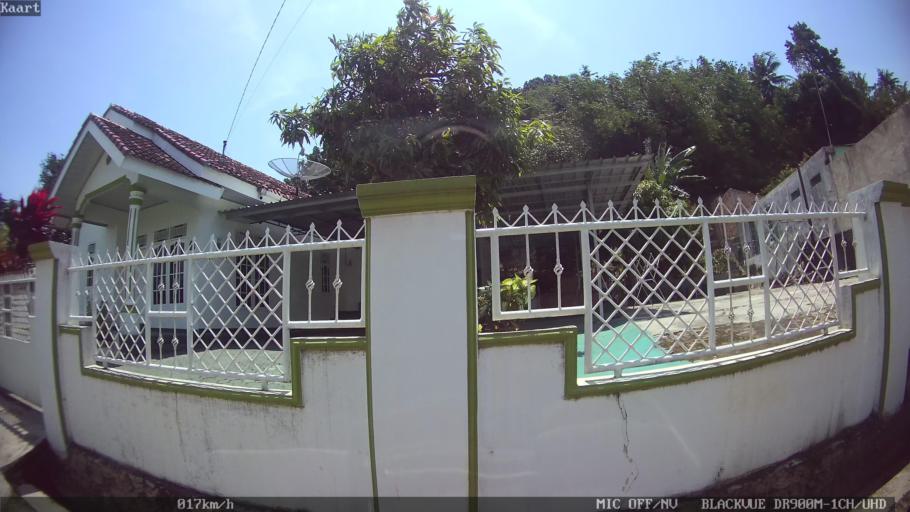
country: ID
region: Lampung
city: Kedaton
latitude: -5.3906
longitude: 105.2711
